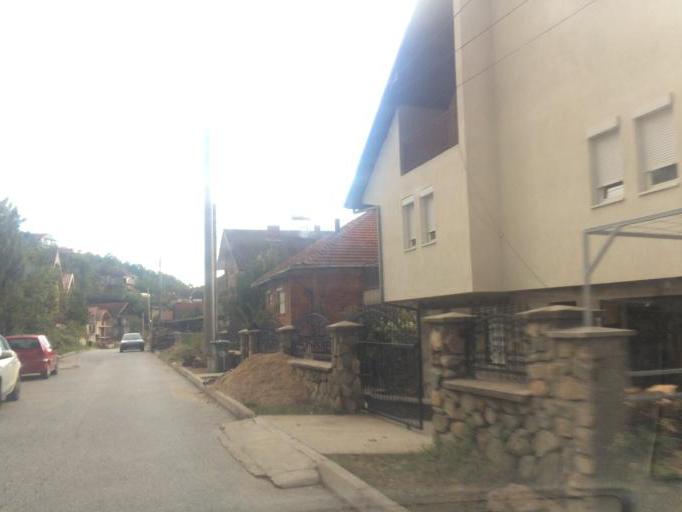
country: MK
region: Makedonska Kamenica
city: Makedonska Kamenica
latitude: 42.0165
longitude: 22.5924
